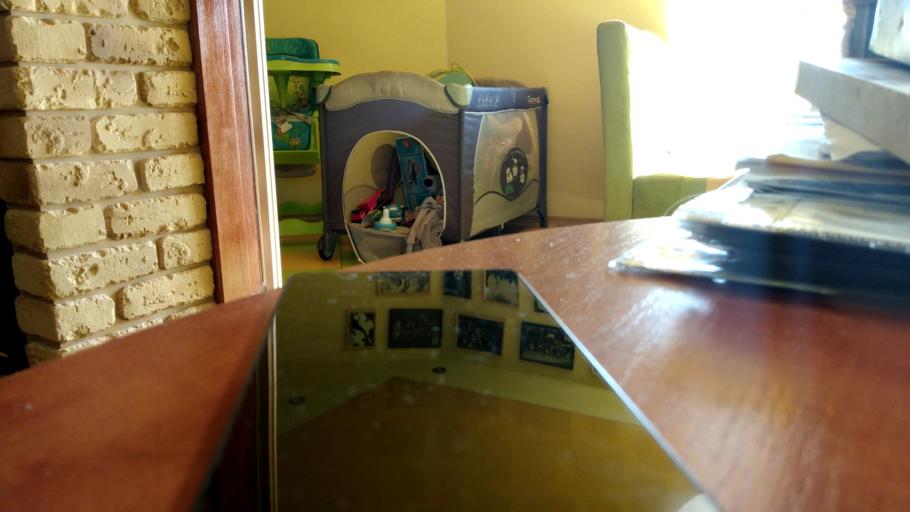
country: RU
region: Penza
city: Serdobsk
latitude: 52.3420
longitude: 44.3685
